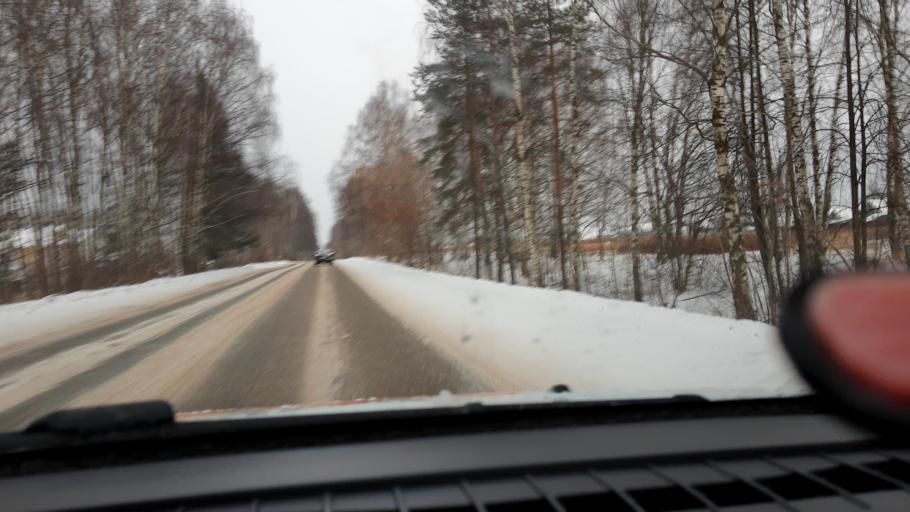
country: RU
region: Nizjnij Novgorod
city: Pamyat' Parizhskoy Kommuny
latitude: 56.2721
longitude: 44.4115
